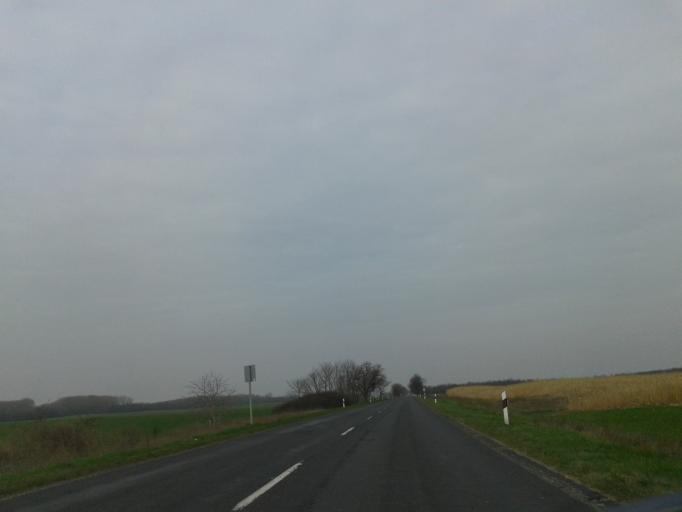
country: HU
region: Komarom-Esztergom
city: Acs
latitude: 47.7276
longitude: 17.9910
